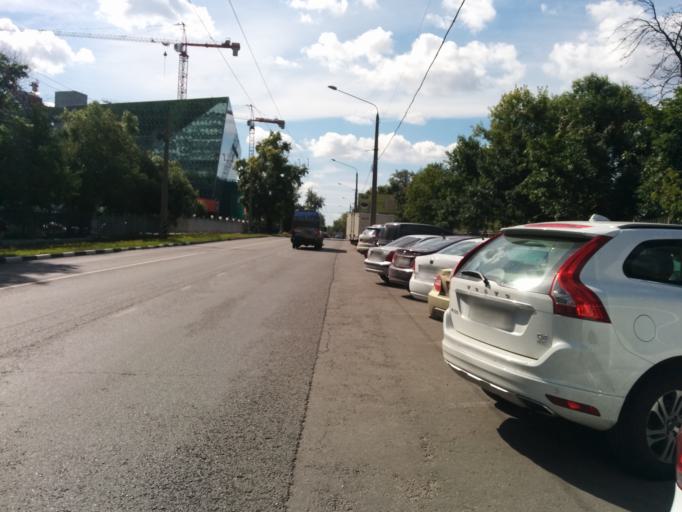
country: RU
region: Moscow
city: Ostankinskiy
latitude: 55.8197
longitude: 37.6167
